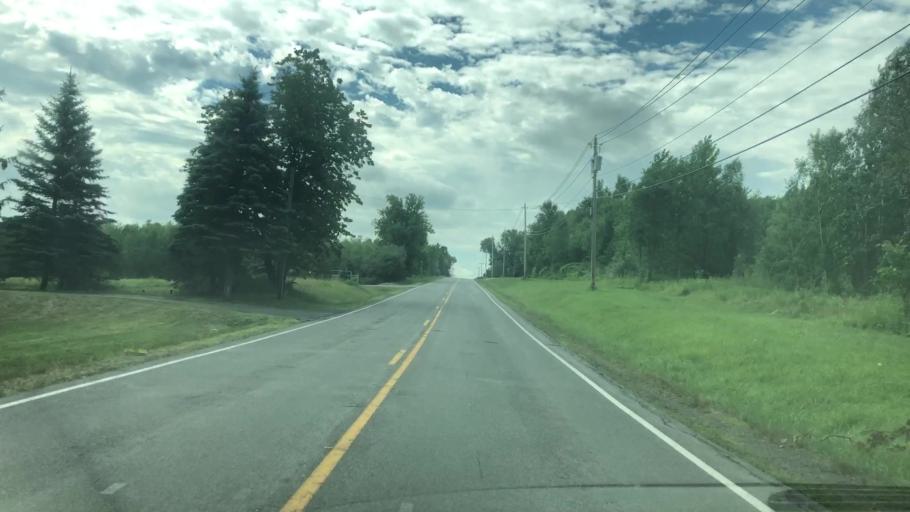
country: US
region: New York
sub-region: Monroe County
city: Fairport
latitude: 43.0718
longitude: -77.3922
